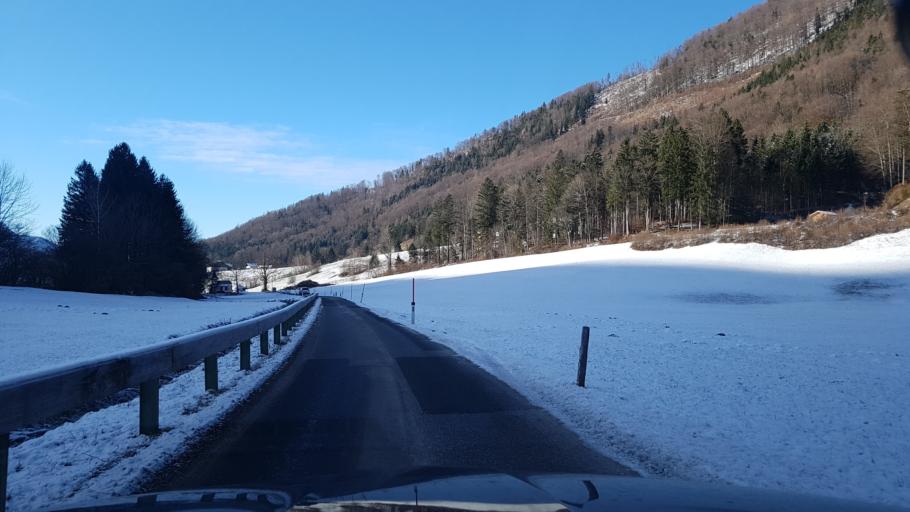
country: AT
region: Salzburg
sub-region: Politischer Bezirk Salzburg-Umgebung
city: Ebenau
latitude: 47.7787
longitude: 13.1481
